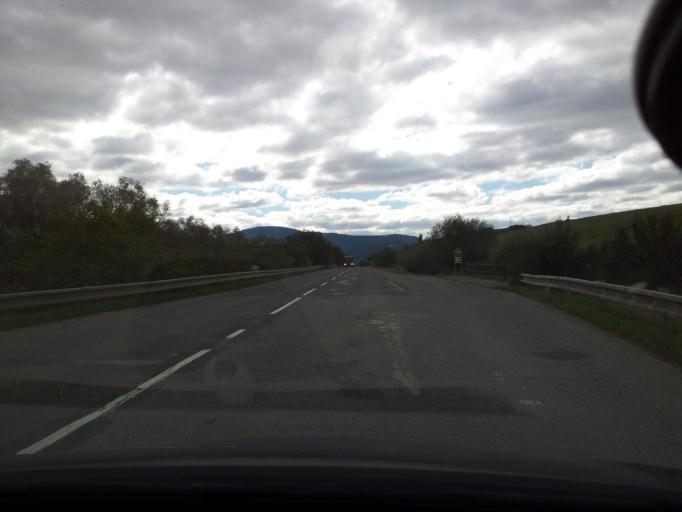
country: SK
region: Zilinsky
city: Ruzomberok
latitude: 49.0926
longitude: 19.4354
